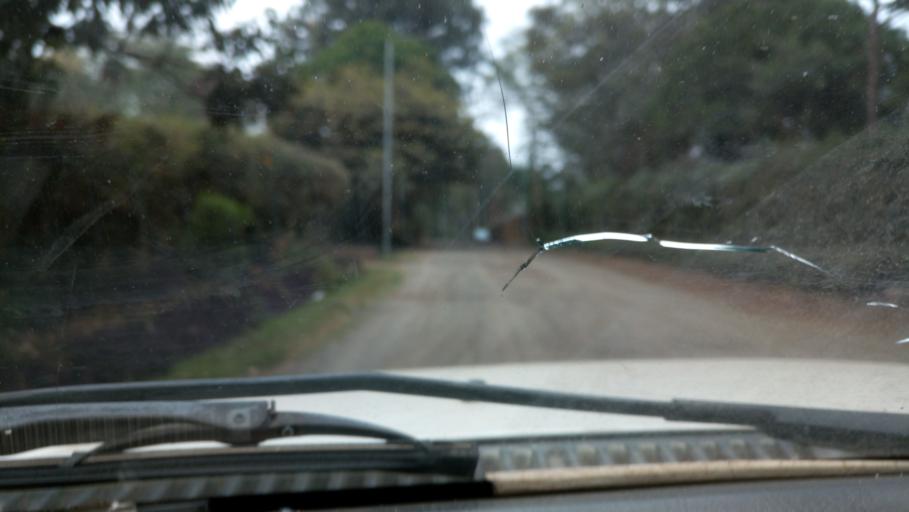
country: KE
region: Nairobi Area
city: Nairobi
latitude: -1.2940
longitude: 36.7789
